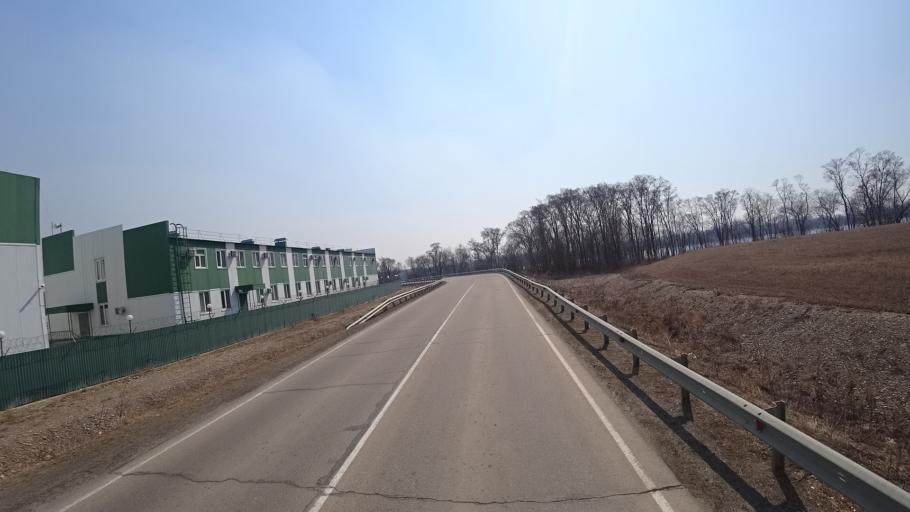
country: RU
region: Amur
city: Novobureyskiy
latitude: 49.7841
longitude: 129.9221
